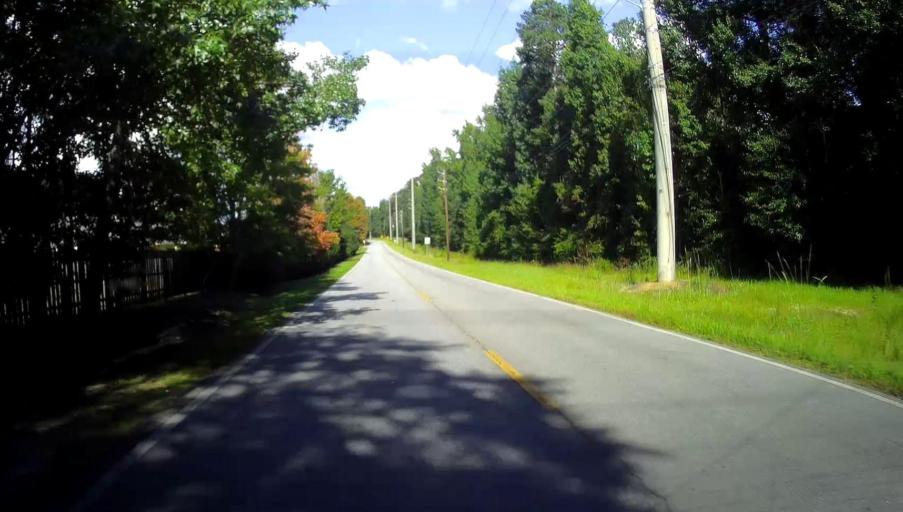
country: US
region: Georgia
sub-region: Muscogee County
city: Columbus
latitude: 32.5522
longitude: -84.8751
